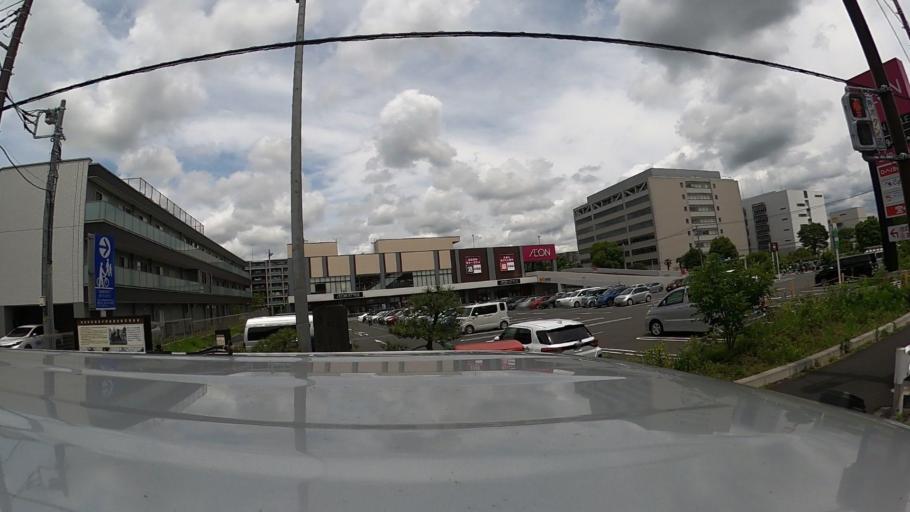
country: JP
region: Kanagawa
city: Fujisawa
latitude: 35.4086
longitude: 139.5391
